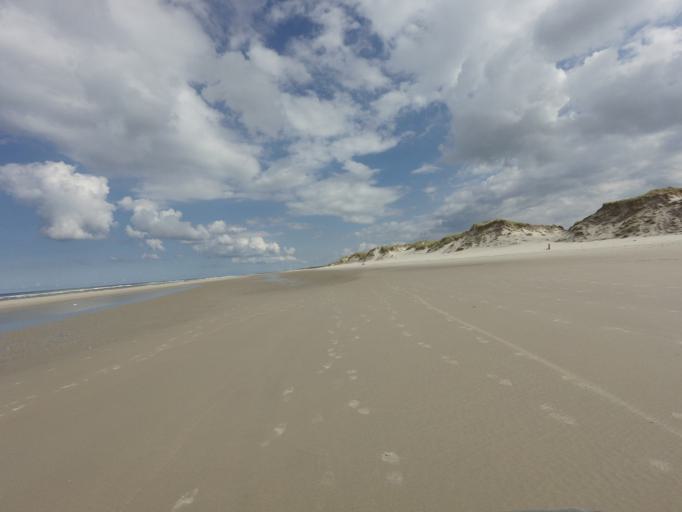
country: NL
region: Friesland
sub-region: Gemeente Terschelling
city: West-Terschelling
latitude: 53.4002
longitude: 5.2281
